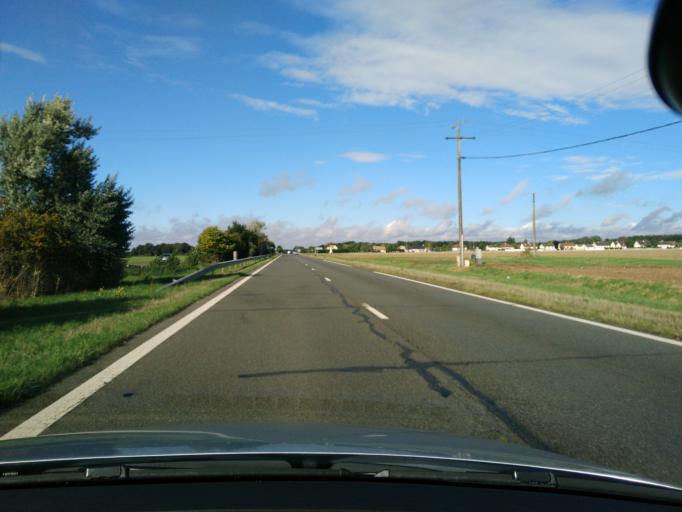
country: FR
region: Centre
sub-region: Departement d'Eure-et-Loir
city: Vert-en-Drouais
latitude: 48.7452
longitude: 1.2836
